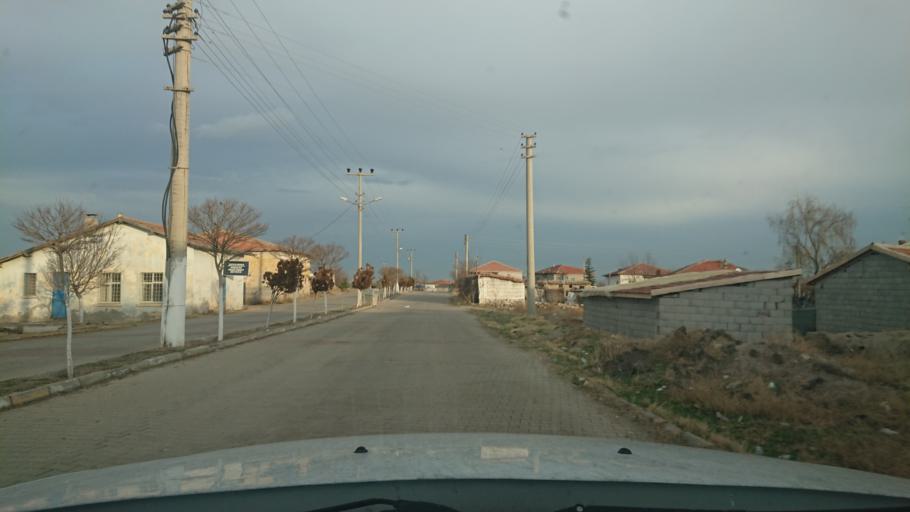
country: TR
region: Aksaray
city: Yesilova
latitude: 38.4132
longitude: 33.8385
